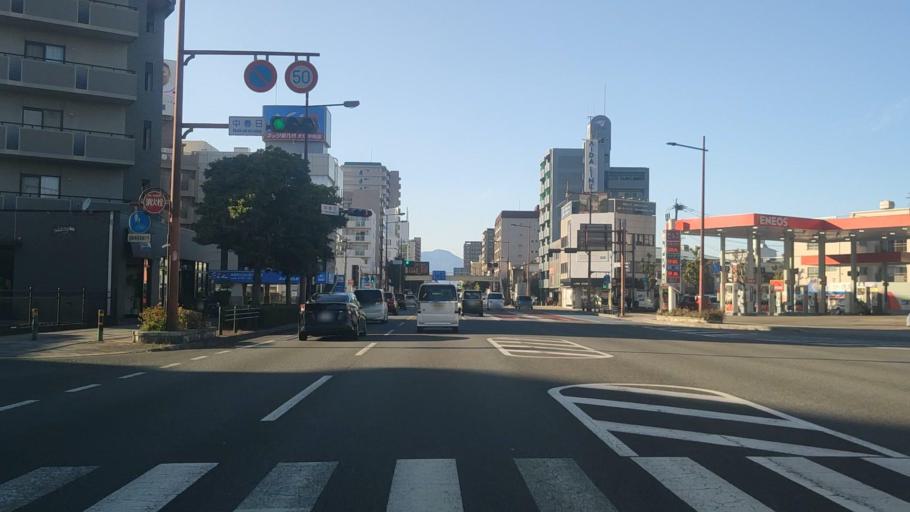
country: JP
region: Oita
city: Oita
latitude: 33.2387
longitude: 131.5987
